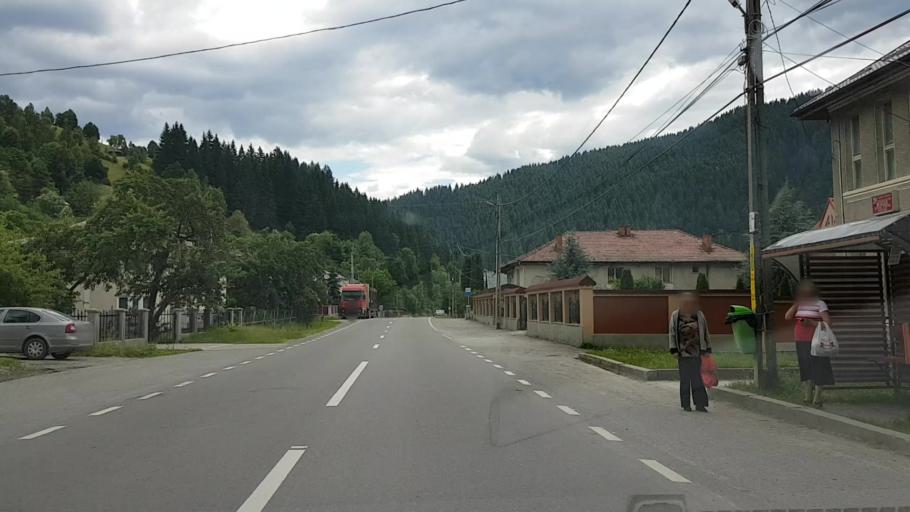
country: RO
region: Neamt
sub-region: Comuna Farcasa
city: Farcasa
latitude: 47.1553
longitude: 25.8406
